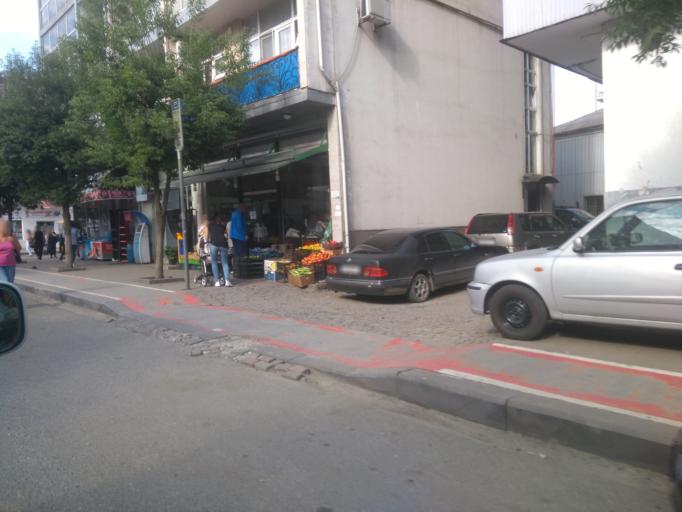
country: GE
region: Ajaria
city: Batumi
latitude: 41.6428
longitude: 41.6235
